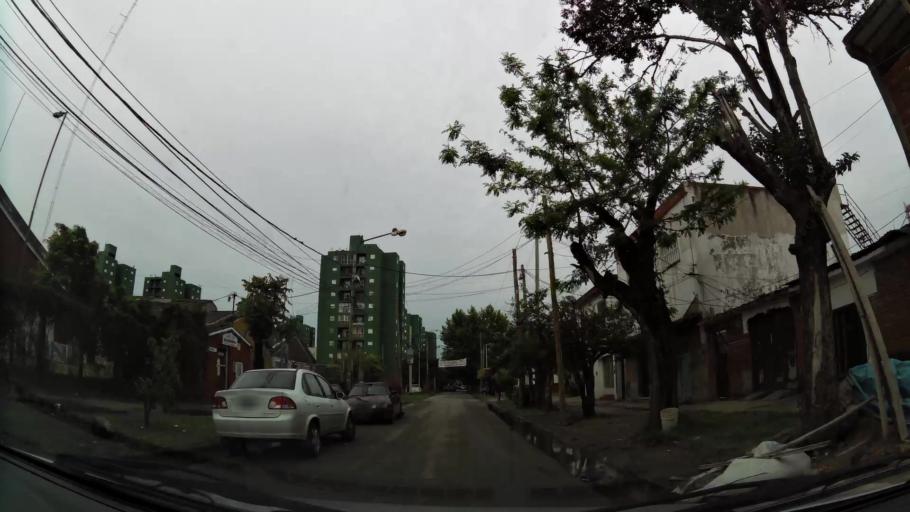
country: AR
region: Buenos Aires
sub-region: Partido de Lanus
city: Lanus
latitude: -34.7113
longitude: -58.3557
